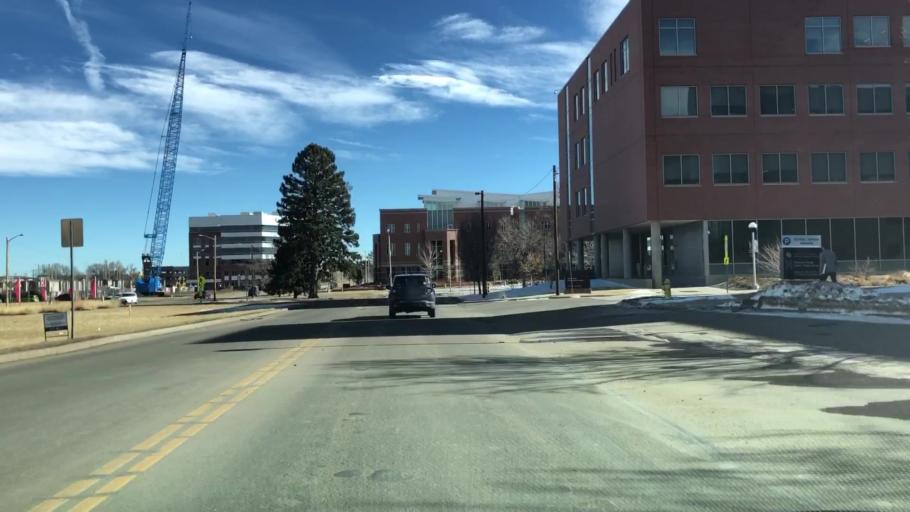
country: US
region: Colorado
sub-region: Adams County
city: Aurora
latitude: 39.7473
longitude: -104.8391
